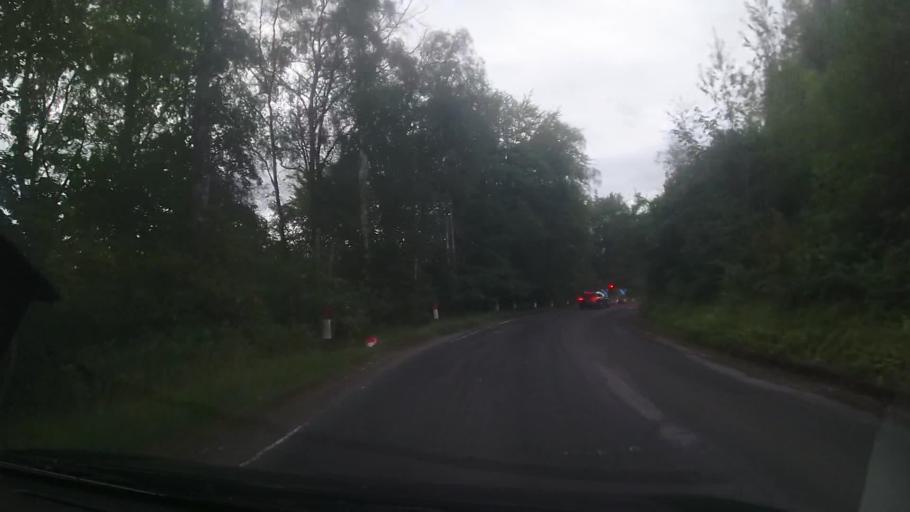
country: GB
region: Scotland
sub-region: Argyll and Bute
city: Garelochhead
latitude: 56.2370
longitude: -5.0790
